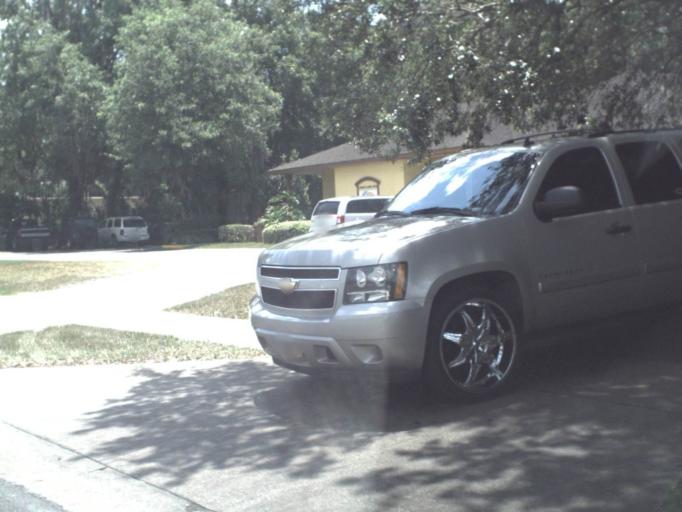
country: US
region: Florida
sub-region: Putnam County
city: Palatka
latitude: 29.6415
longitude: -81.6648
